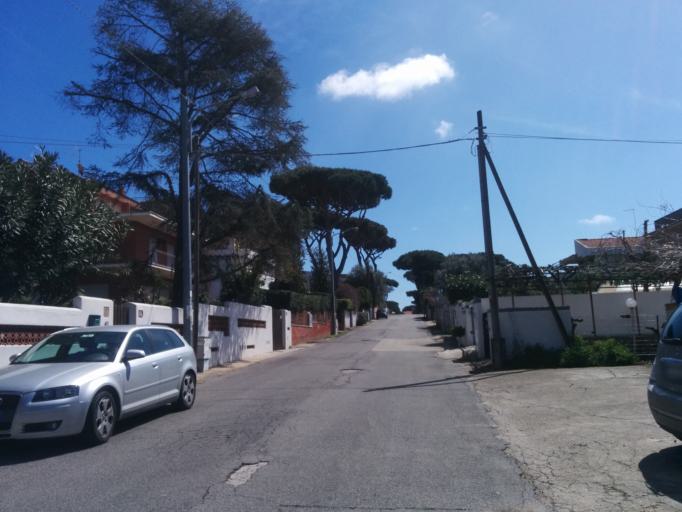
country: IT
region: Latium
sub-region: Citta metropolitana di Roma Capitale
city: Lavinio
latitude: 41.4997
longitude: 12.5966
